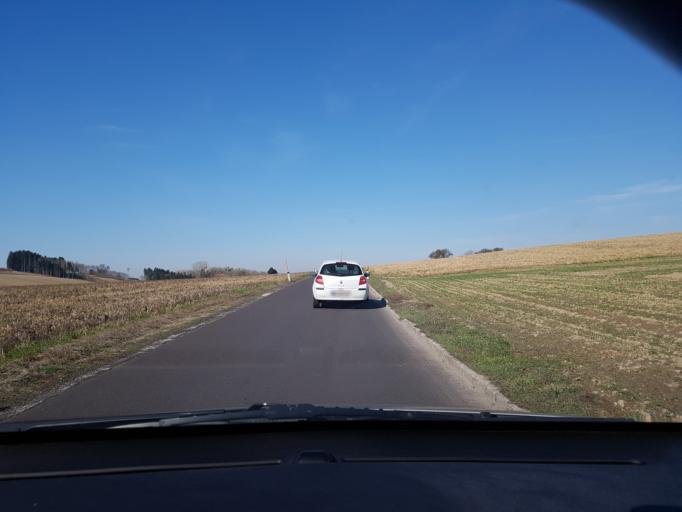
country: AT
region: Upper Austria
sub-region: Politischer Bezirk Linz-Land
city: Ansfelden
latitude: 48.2050
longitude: 14.3028
